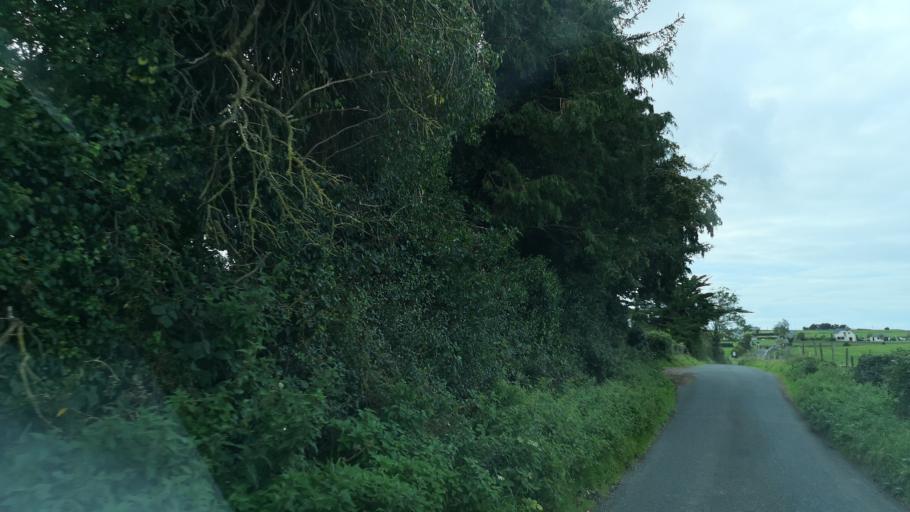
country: IE
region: Connaught
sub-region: County Galway
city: Ballinasloe
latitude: 53.3752
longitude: -8.1689
